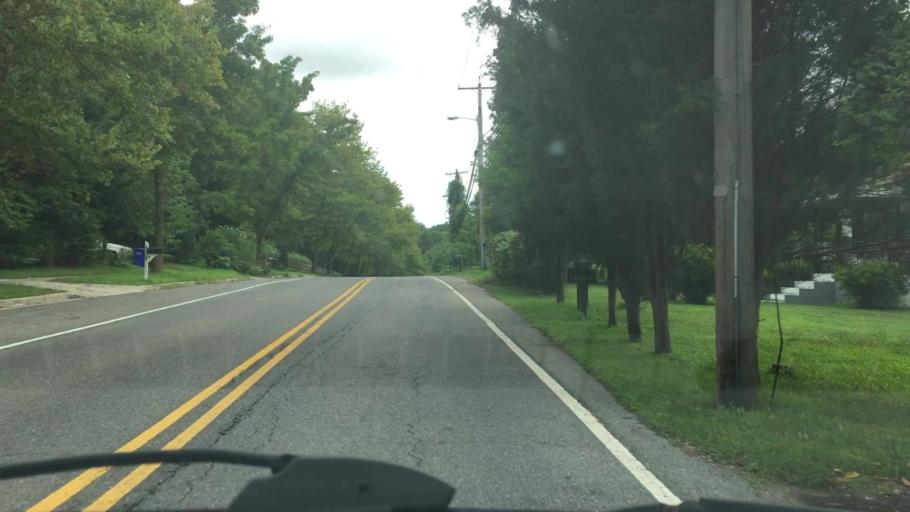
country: US
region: Maryland
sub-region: Prince George's County
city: Glenn Dale
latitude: 39.0007
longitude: -76.7782
